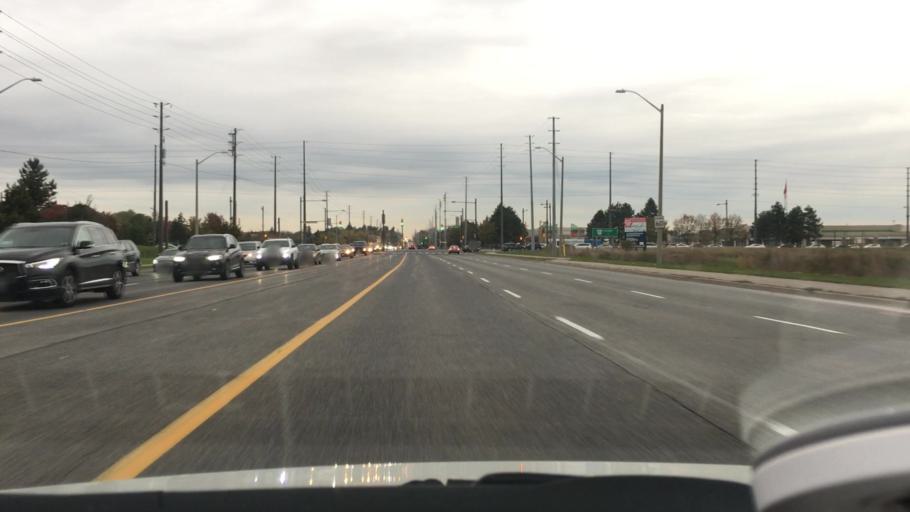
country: CA
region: Ontario
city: Markham
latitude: 43.8541
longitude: -79.3335
